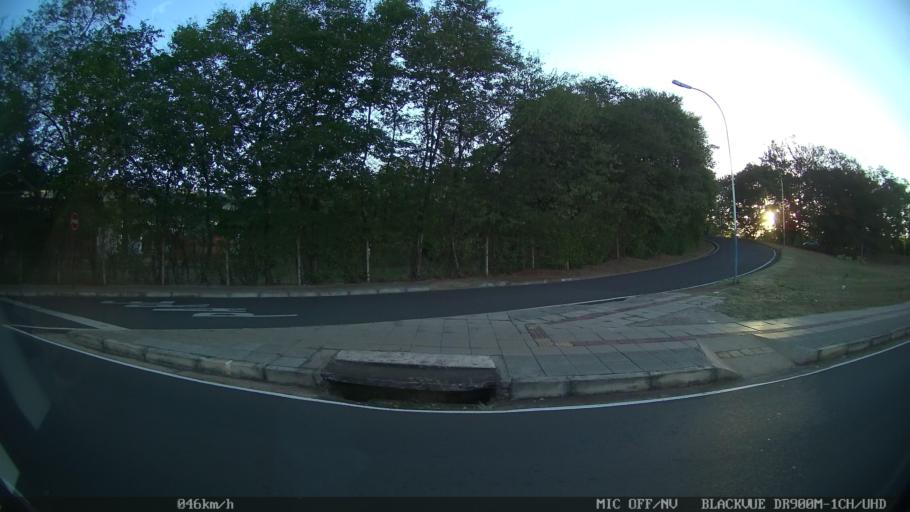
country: BR
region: Sao Paulo
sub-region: Sao Jose Do Rio Preto
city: Sao Jose do Rio Preto
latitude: -20.8026
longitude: -49.3781
